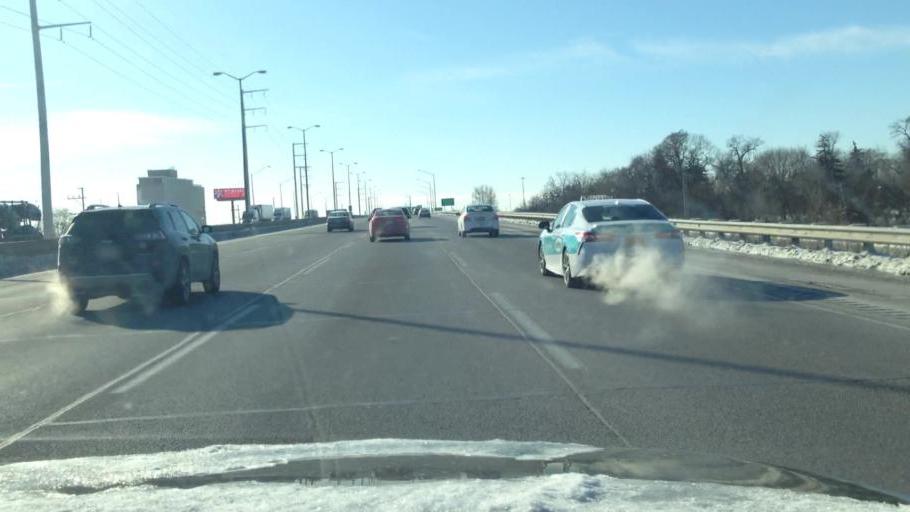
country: US
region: Illinois
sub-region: DuPage County
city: Elmhurst
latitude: 41.9112
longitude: -87.9202
